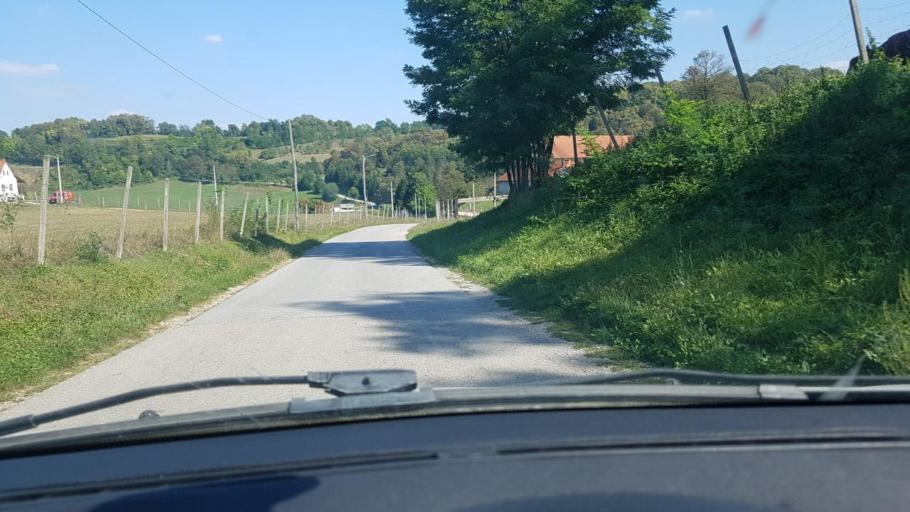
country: HR
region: Karlovacka
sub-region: Grad Karlovac
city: Karlovac
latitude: 45.4784
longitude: 15.4443
